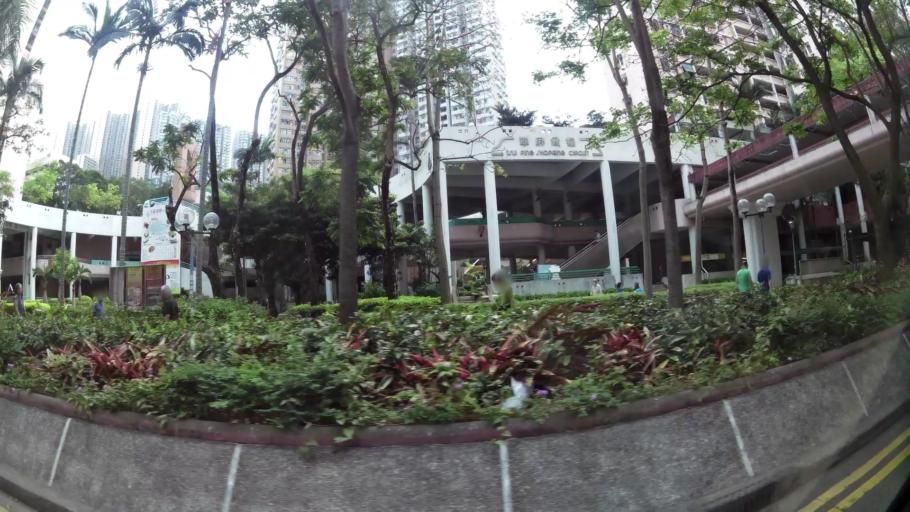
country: HK
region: Kowloon City
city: Kowloon
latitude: 22.3147
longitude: 114.2296
